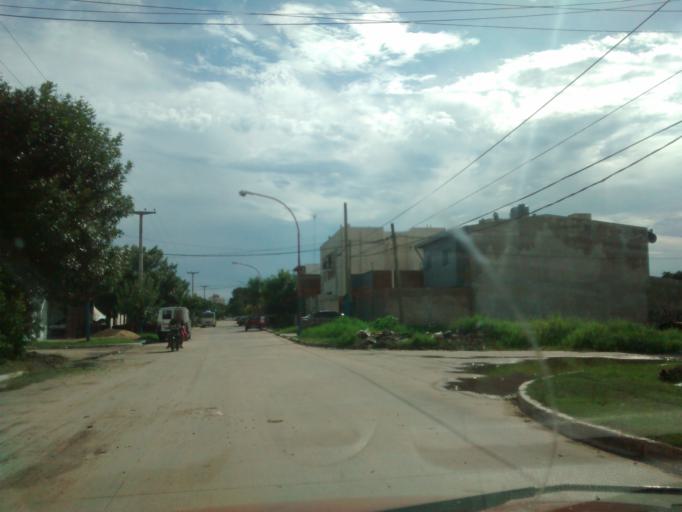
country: AR
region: Chaco
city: Resistencia
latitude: -27.4368
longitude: -58.9901
